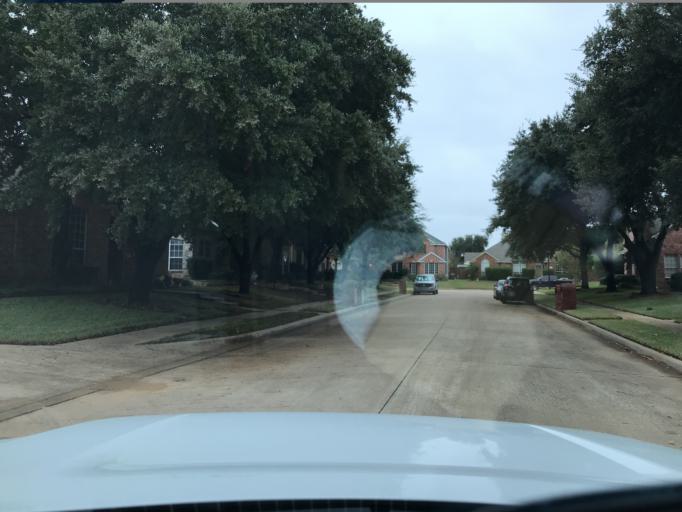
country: US
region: Texas
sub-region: Denton County
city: Highland Village
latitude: 33.0833
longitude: -97.0293
